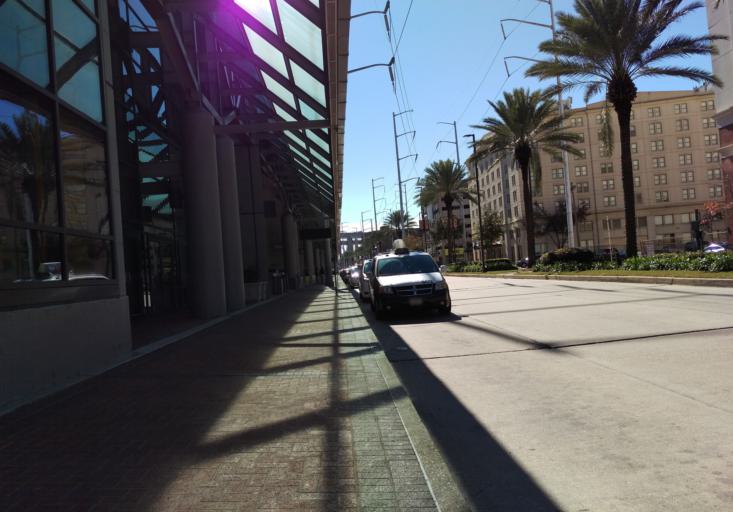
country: US
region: Louisiana
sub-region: Orleans Parish
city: New Orleans
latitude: 29.9434
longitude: -90.0646
